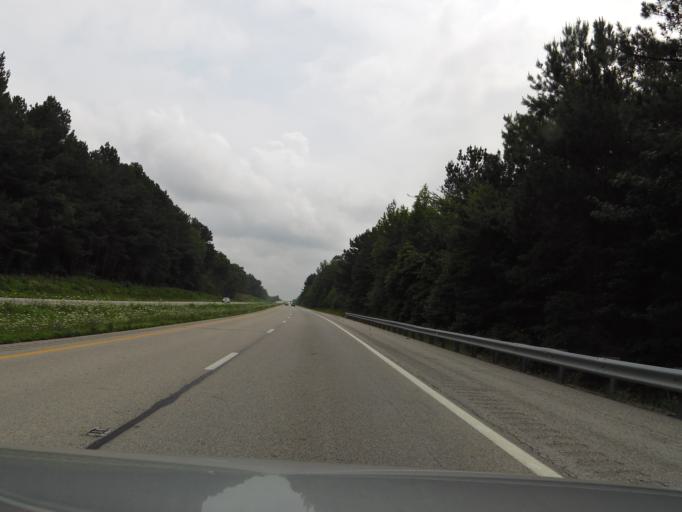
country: US
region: Kentucky
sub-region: Ohio County
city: Beaver Dam
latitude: 37.3523
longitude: -86.8917
